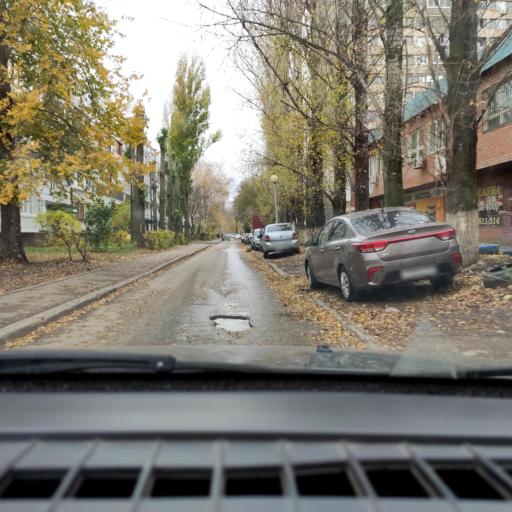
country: RU
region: Samara
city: Tol'yatti
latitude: 53.5267
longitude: 49.2907
